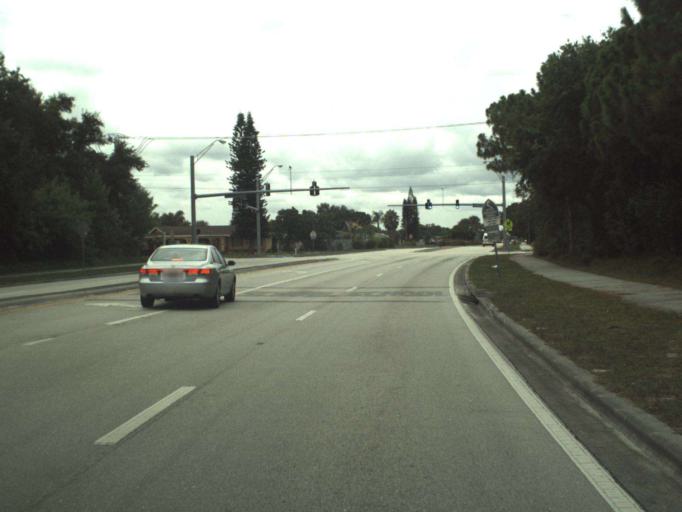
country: US
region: Florida
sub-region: Saint Lucie County
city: River Park
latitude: 27.3266
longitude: -80.3498
